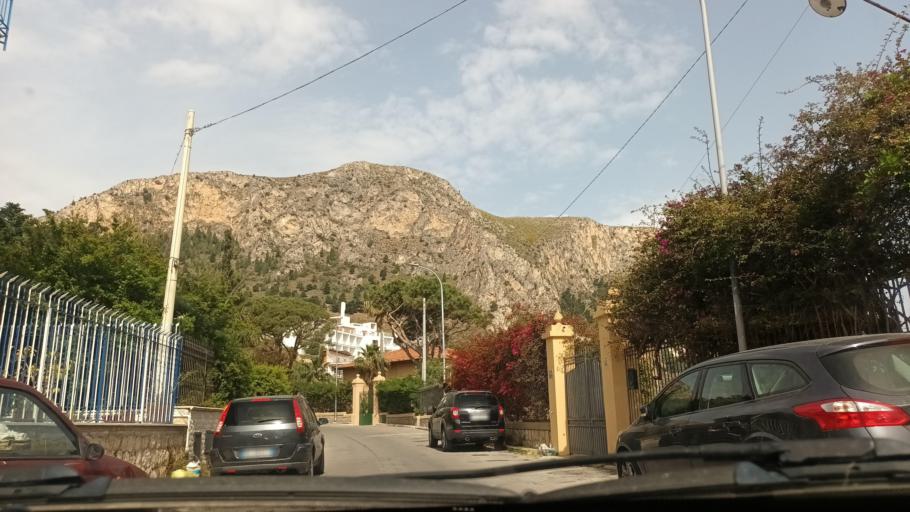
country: IT
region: Sicily
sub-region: Palermo
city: Santa Flavia
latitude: 38.0974
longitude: 13.5379
